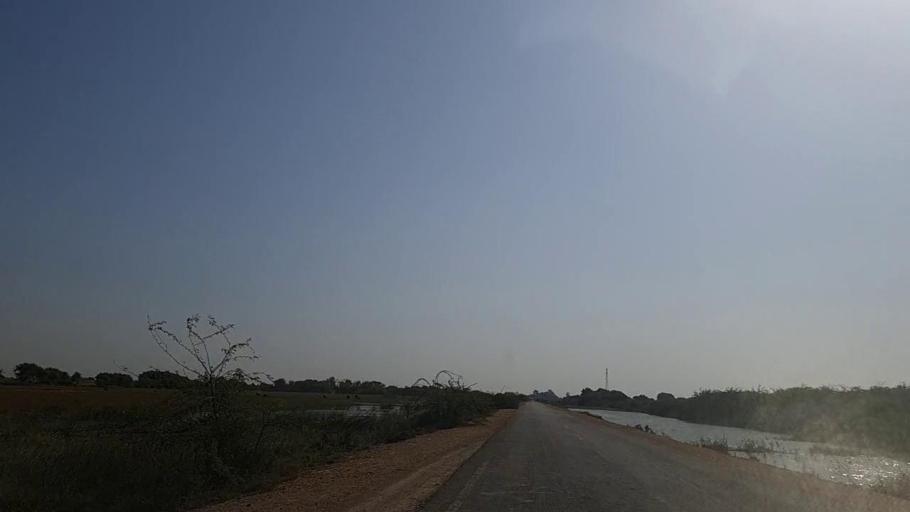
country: PK
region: Sindh
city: Jati
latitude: 24.5252
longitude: 68.2770
